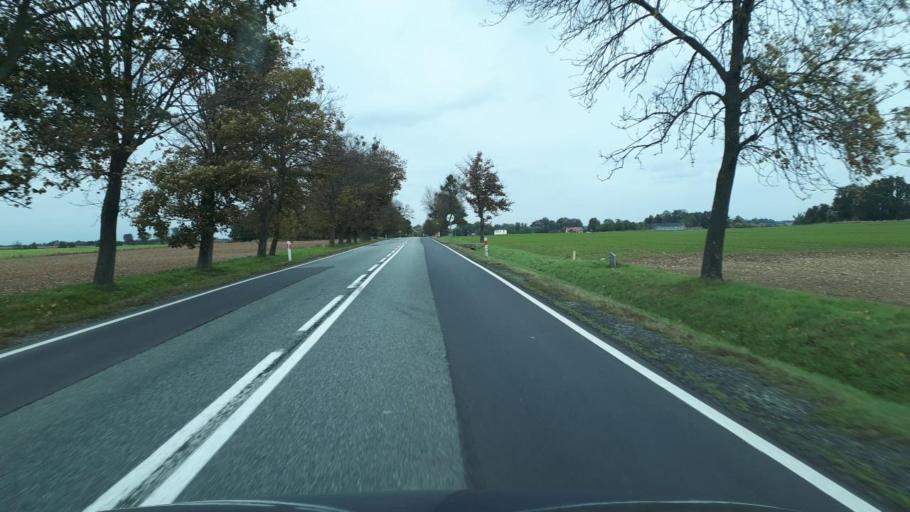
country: PL
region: Opole Voivodeship
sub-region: Powiat kluczborski
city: Byczyna
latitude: 51.0540
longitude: 18.1974
